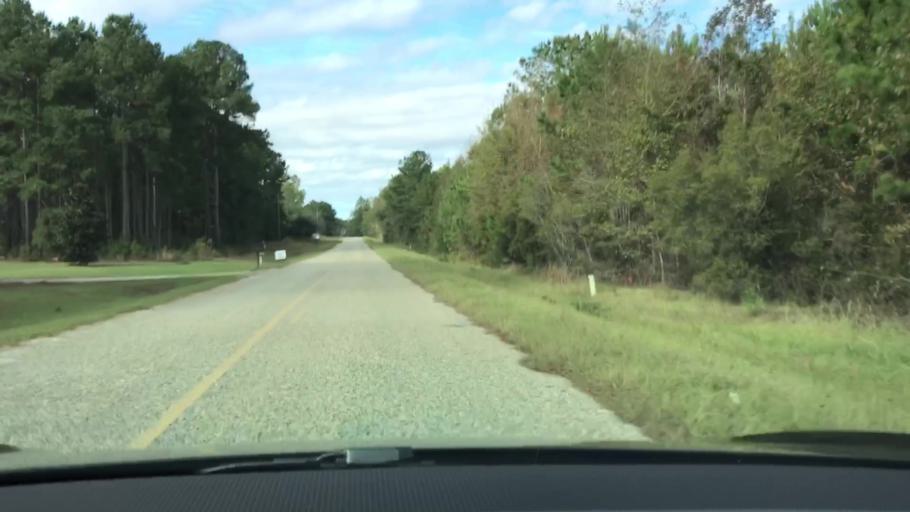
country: US
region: Georgia
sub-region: Jefferson County
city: Wadley
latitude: 32.8096
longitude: -82.3409
